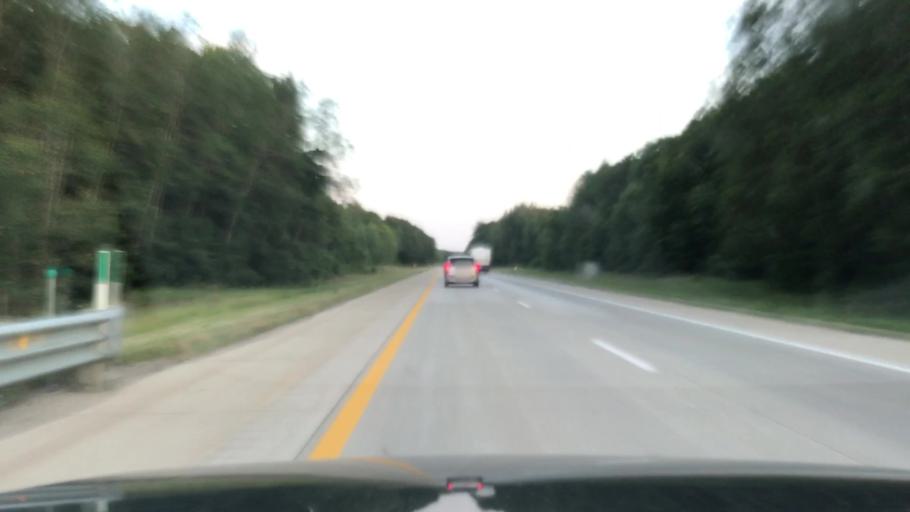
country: US
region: Michigan
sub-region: Montcalm County
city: Howard City
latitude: 43.3593
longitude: -85.5140
